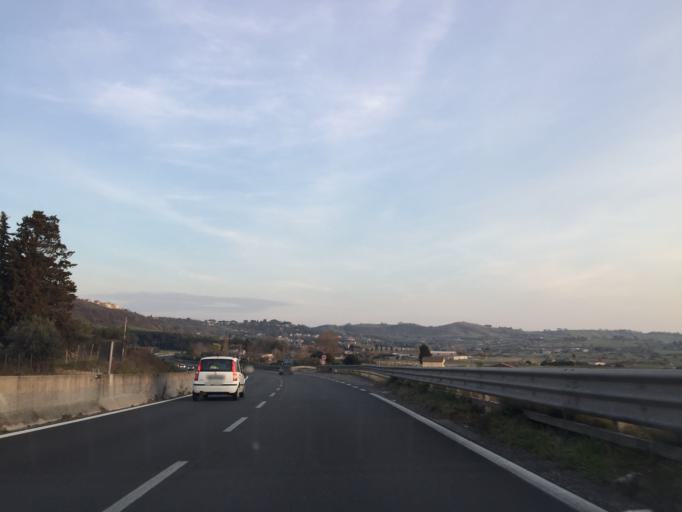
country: IT
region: Latium
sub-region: Citta metropolitana di Roma Capitale
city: Campagnano di Roma
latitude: 42.1307
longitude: 12.3570
